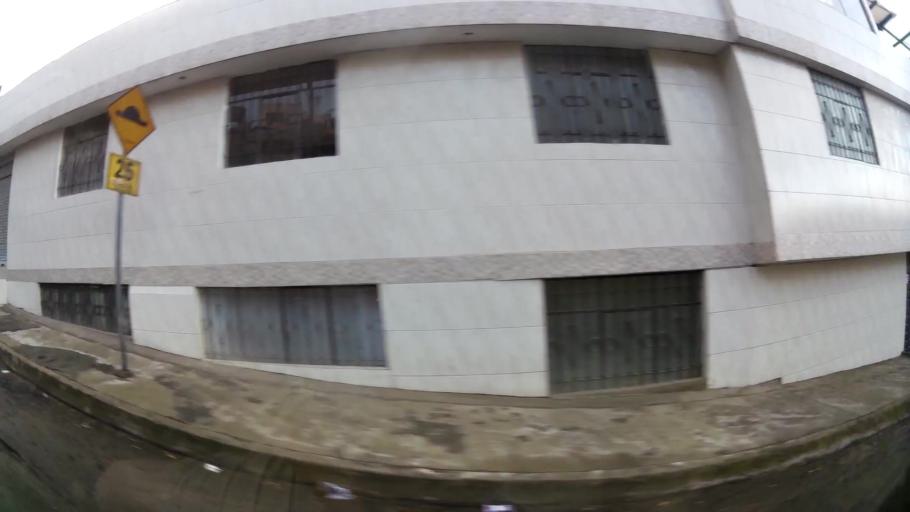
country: EC
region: Pichincha
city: Quito
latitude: -0.1180
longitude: -78.5130
